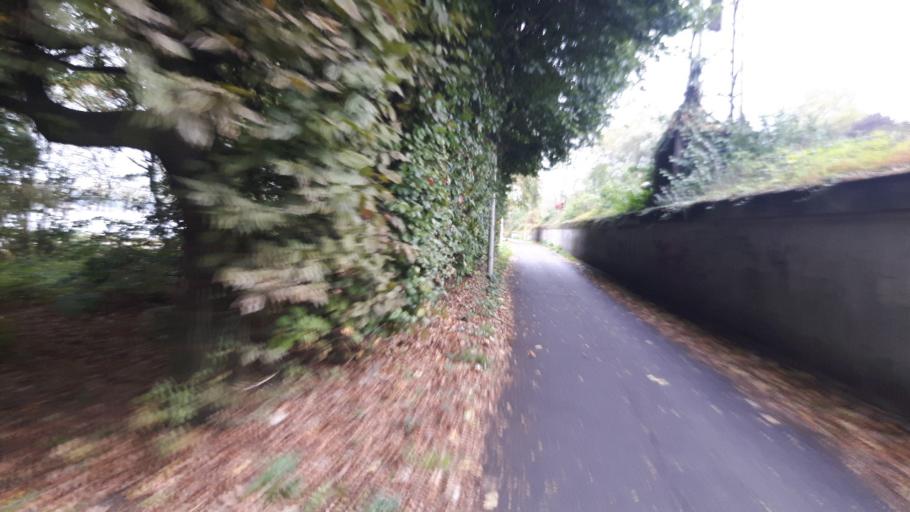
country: DE
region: North Rhine-Westphalia
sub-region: Regierungsbezirk Koln
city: Konigswinter
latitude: 50.7042
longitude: 7.1720
